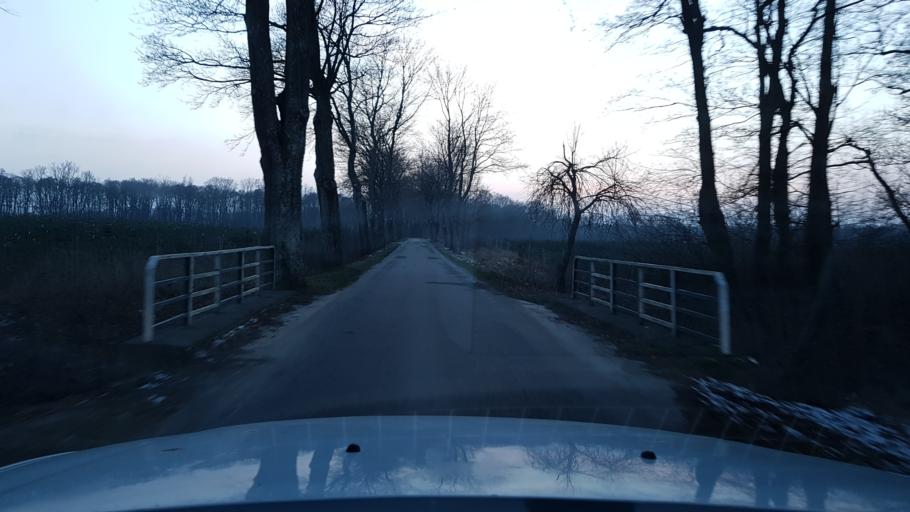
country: PL
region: West Pomeranian Voivodeship
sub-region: Powiat bialogardzki
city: Karlino
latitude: 54.0063
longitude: 15.8349
